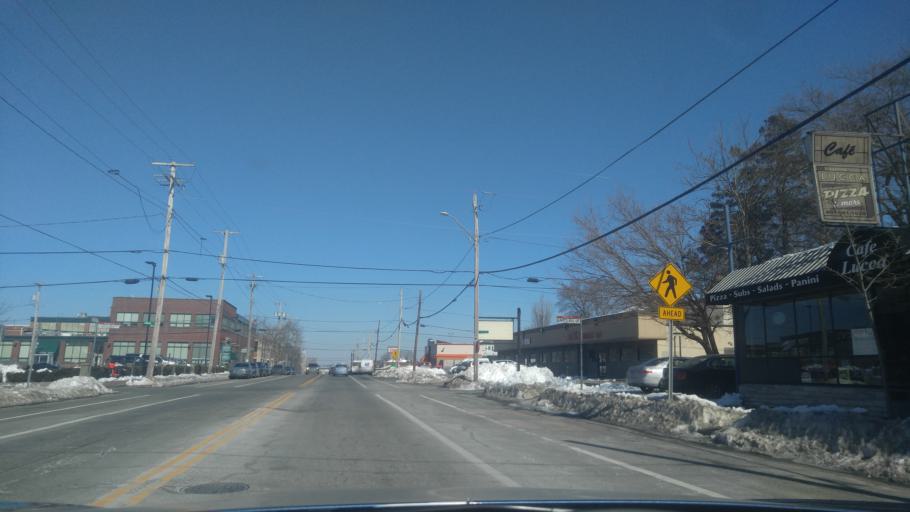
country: US
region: Rhode Island
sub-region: Providence County
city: East Providence
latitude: 41.7913
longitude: -71.3967
